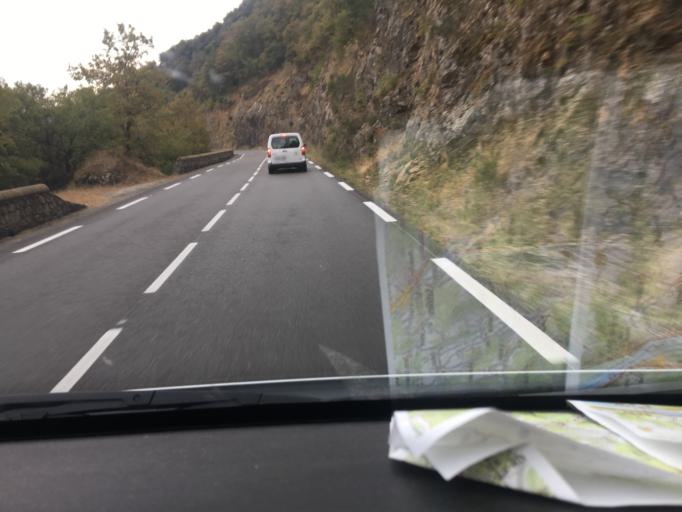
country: FR
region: Rhone-Alpes
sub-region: Departement de l'Ardeche
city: Saint-Jean-de-Muzols
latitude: 45.0620
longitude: 4.7611
